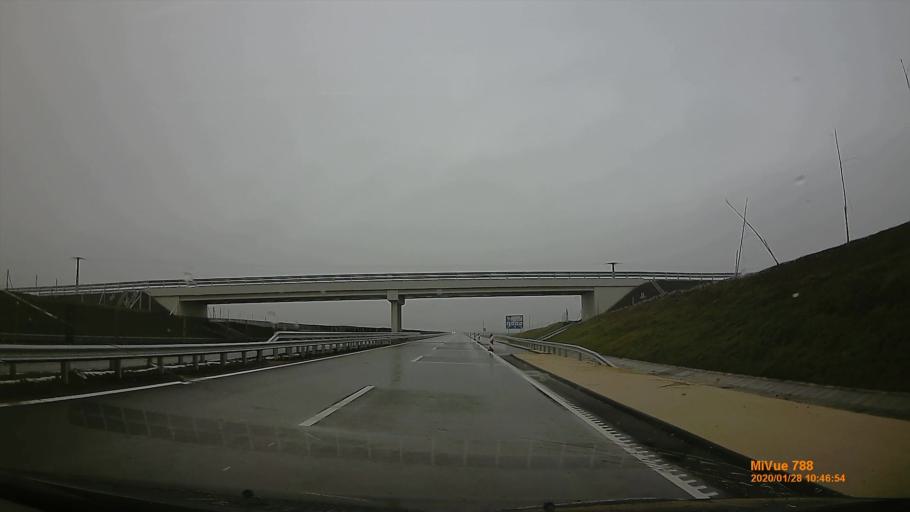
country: HU
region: Pest
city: Monor
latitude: 47.3698
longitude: 19.4769
